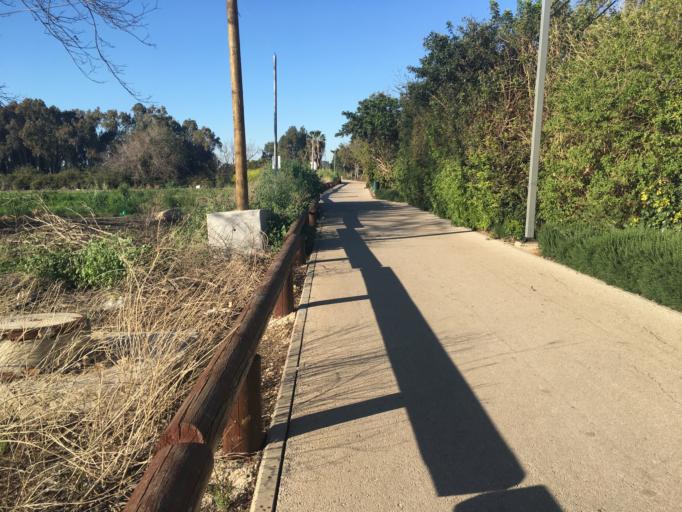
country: IL
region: Tel Aviv
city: Ramat HaSharon
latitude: 32.1427
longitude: 34.8260
